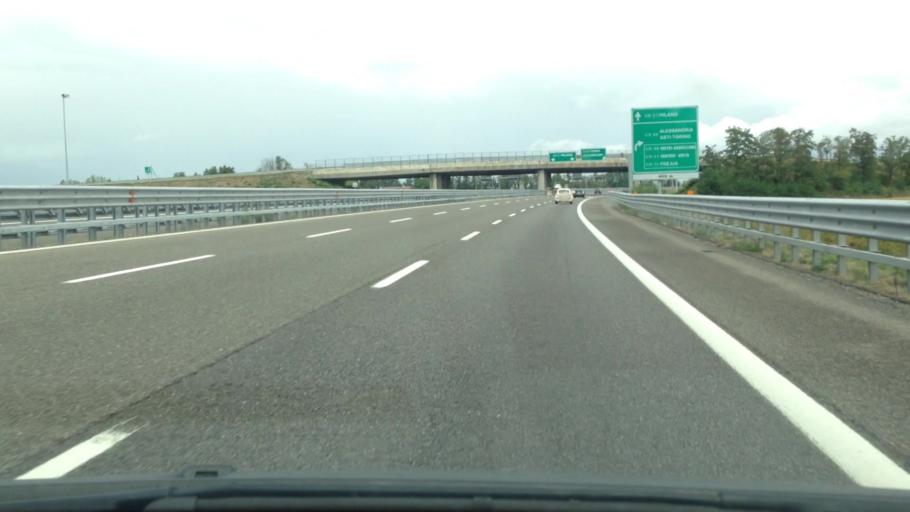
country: IT
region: Piedmont
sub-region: Provincia di Alessandria
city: Tortona
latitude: 44.9186
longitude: 8.8448
